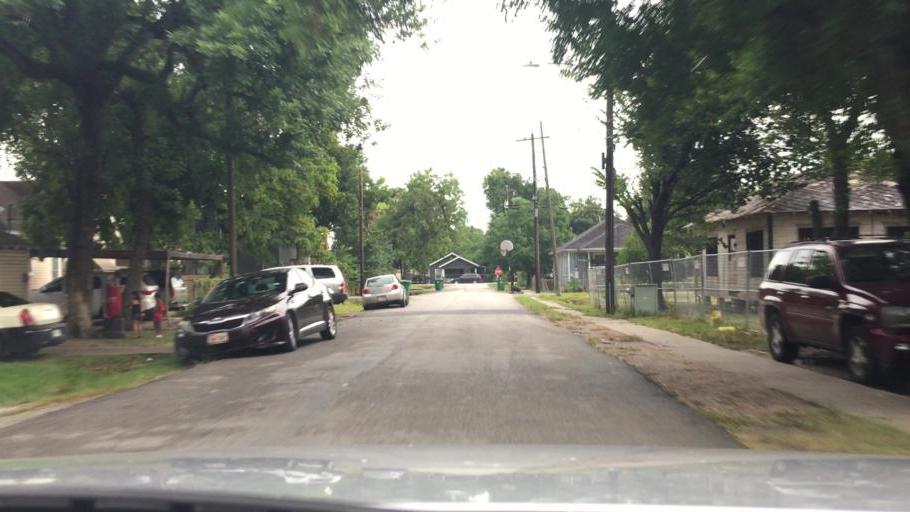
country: US
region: Texas
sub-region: Harris County
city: Houston
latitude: 29.8013
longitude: -95.3698
